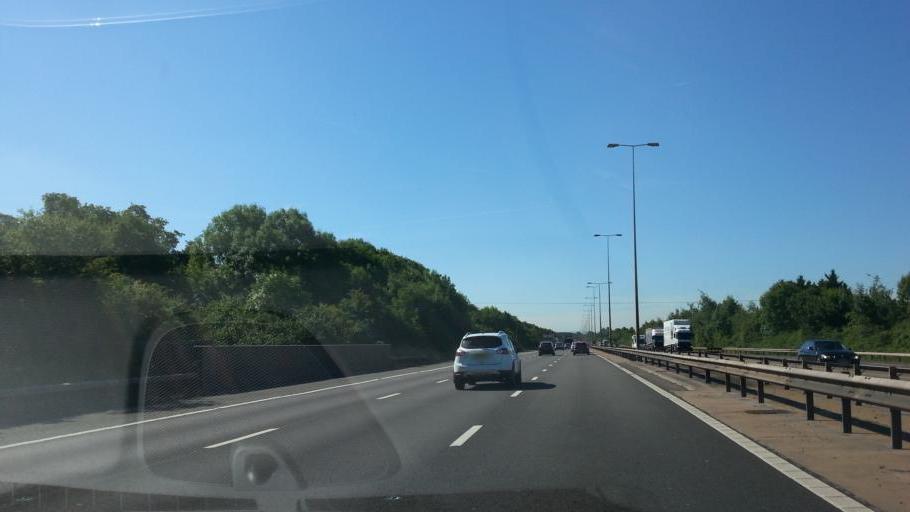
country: GB
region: England
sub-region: Worcestershire
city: Kempsey
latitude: 52.1252
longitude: -2.2001
